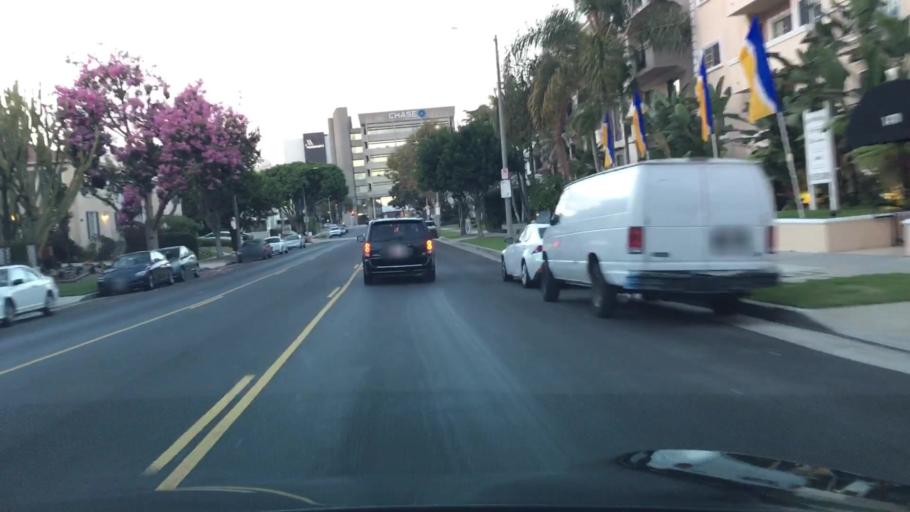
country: US
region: California
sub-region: Los Angeles County
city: Beverly Hills
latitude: 34.0530
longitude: -118.3954
